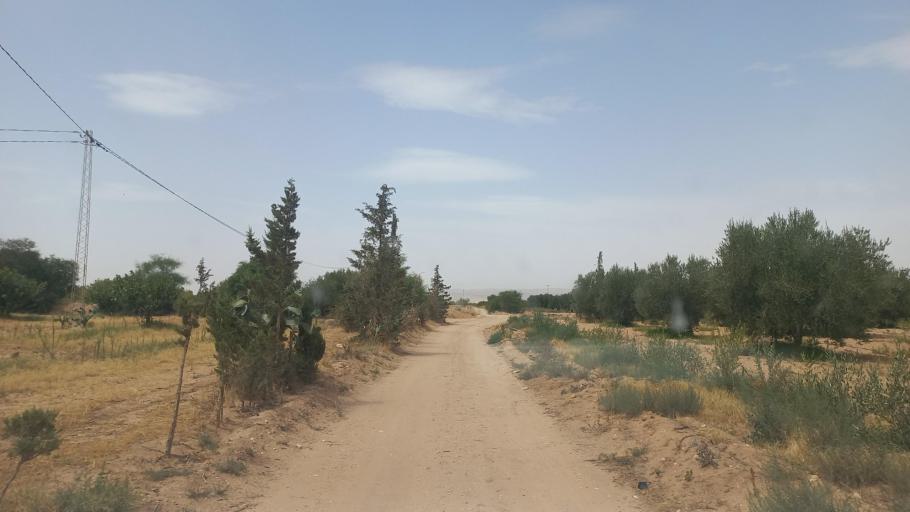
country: TN
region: Al Qasrayn
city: Kasserine
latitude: 35.2580
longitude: 9.0001
